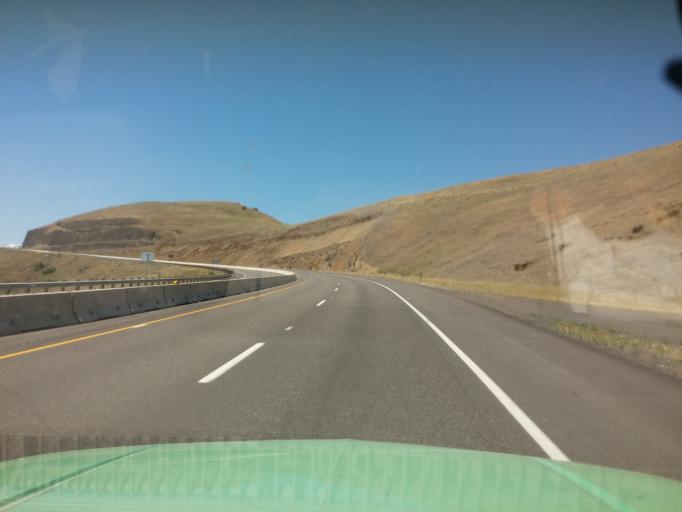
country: US
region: Idaho
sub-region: Nez Perce County
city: Lewiston
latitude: 46.4625
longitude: -116.9821
